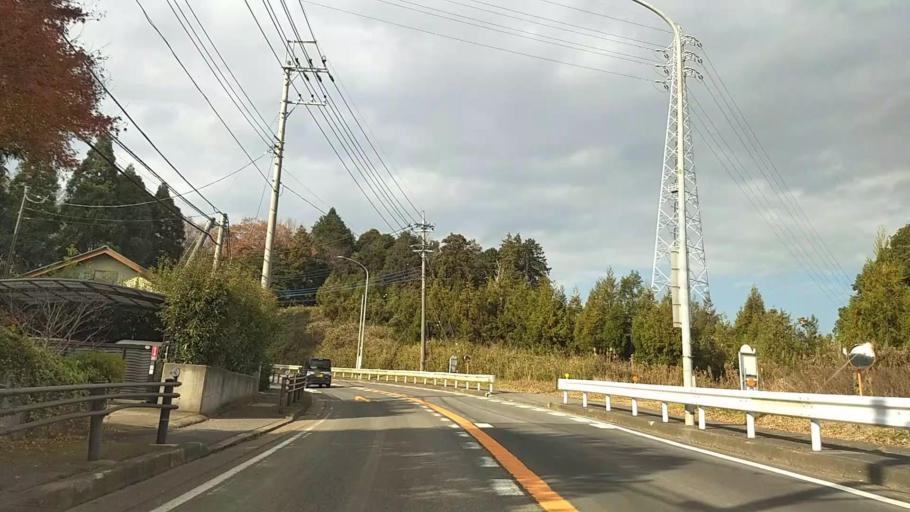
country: JP
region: Chiba
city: Oami
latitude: 35.5752
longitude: 140.3046
